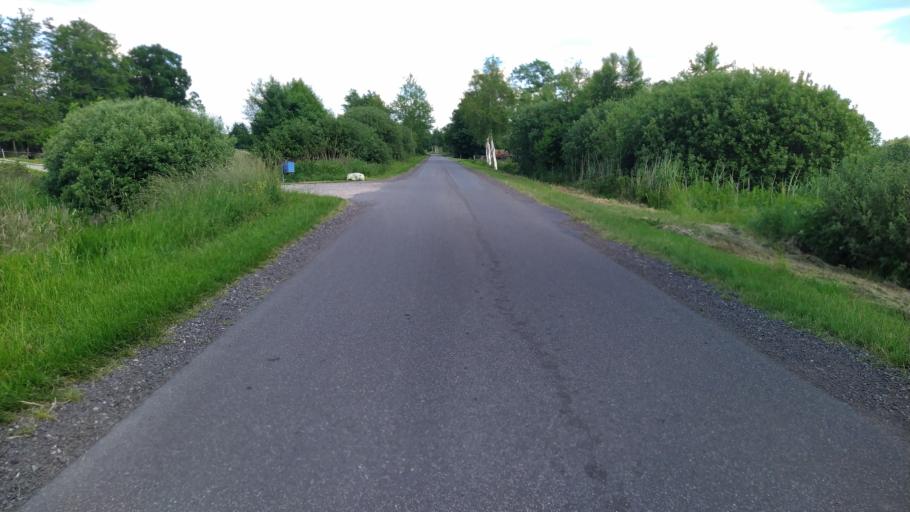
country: DE
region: Lower Saxony
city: Steinau
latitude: 53.6561
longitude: 8.9008
